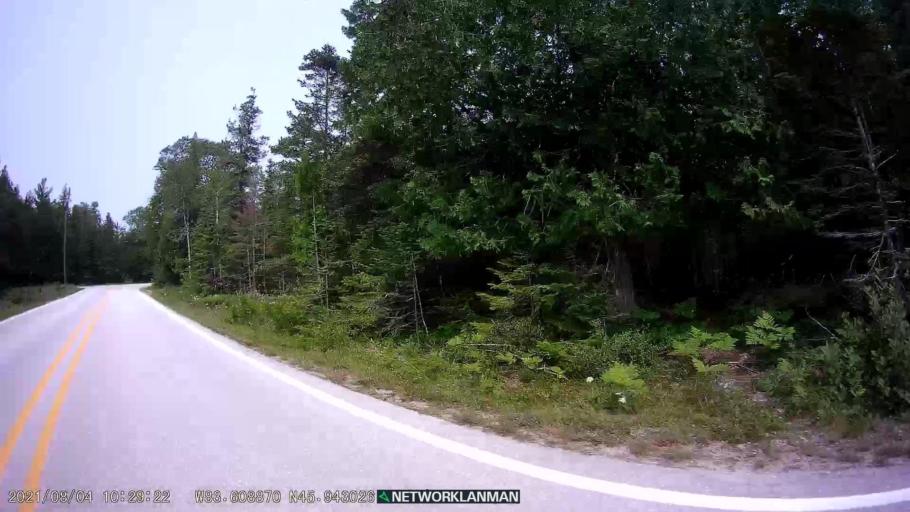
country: CA
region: Ontario
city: Thessalon
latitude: 45.9431
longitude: -83.6090
